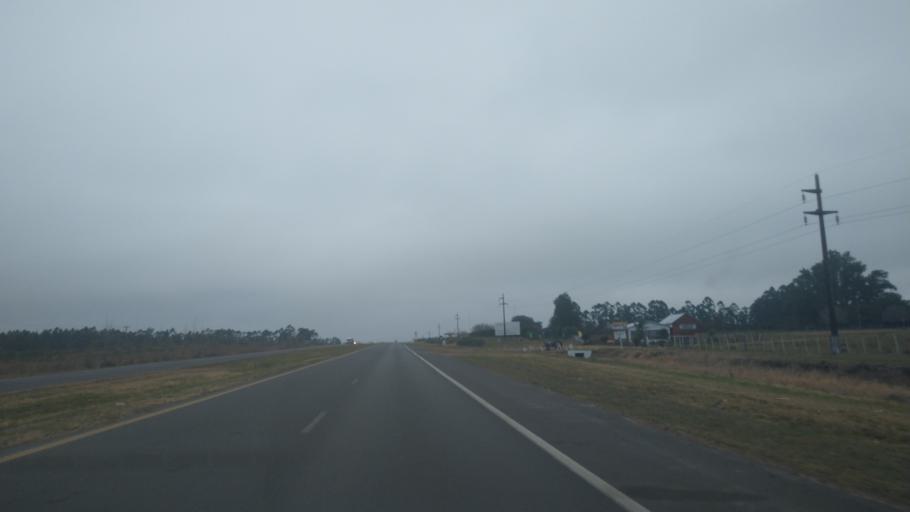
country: AR
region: Entre Rios
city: Chajari
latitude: -30.8148
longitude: -58.0418
